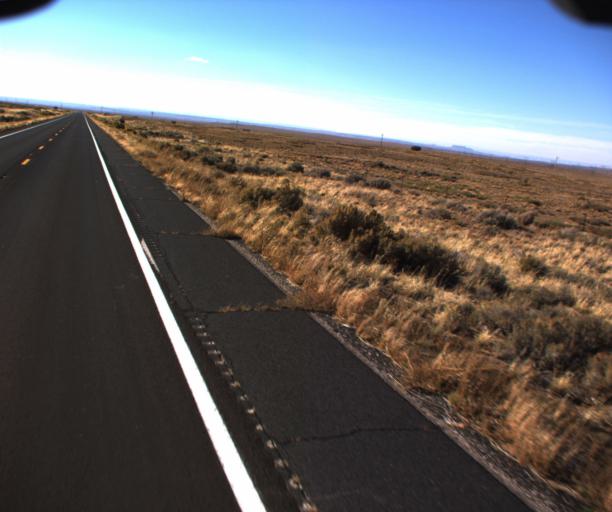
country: US
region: Arizona
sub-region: Coconino County
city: Kaibito
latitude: 36.6156
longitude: -110.9365
